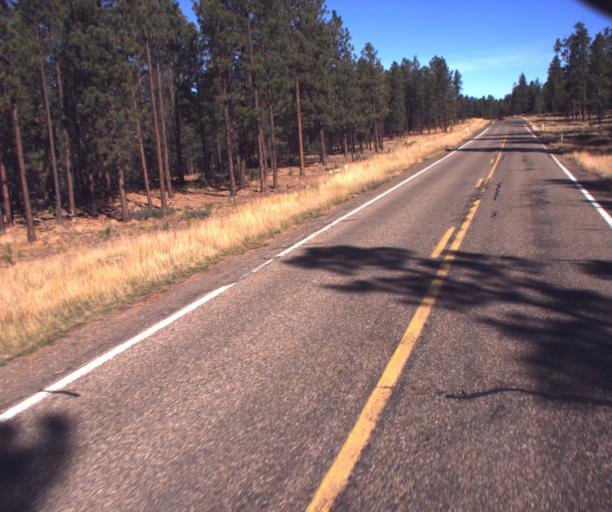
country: US
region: Arizona
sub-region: Coconino County
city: Fredonia
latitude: 36.7290
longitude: -112.2123
